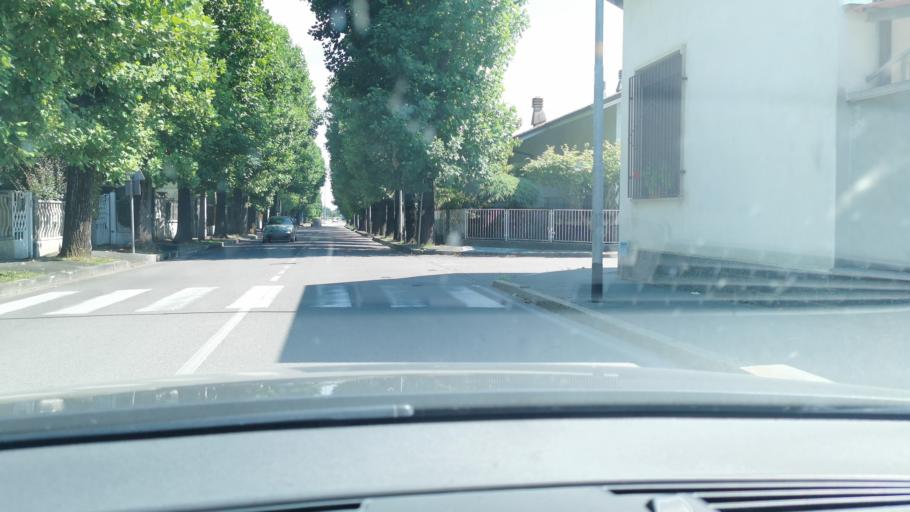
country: IT
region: Lombardy
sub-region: Citta metropolitana di Milano
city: Rescaldina
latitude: 45.6182
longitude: 8.9559
